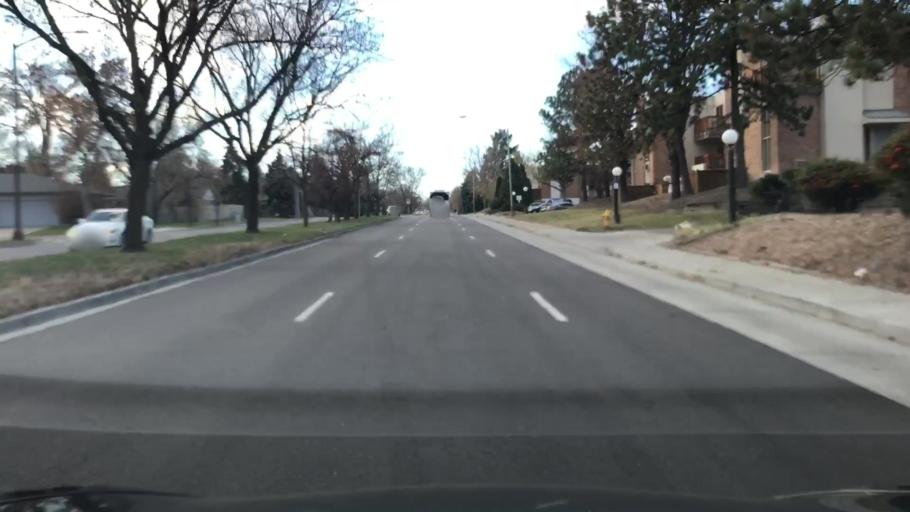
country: US
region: Colorado
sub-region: Arapahoe County
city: Glendale
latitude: 39.6657
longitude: -104.9131
